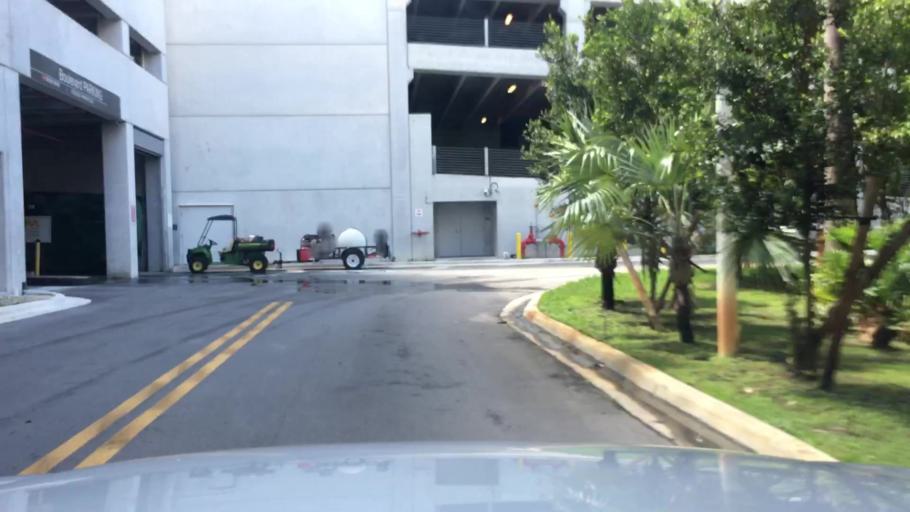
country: US
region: Florida
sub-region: Miami-Dade County
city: Doral
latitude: 25.8083
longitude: -80.3320
